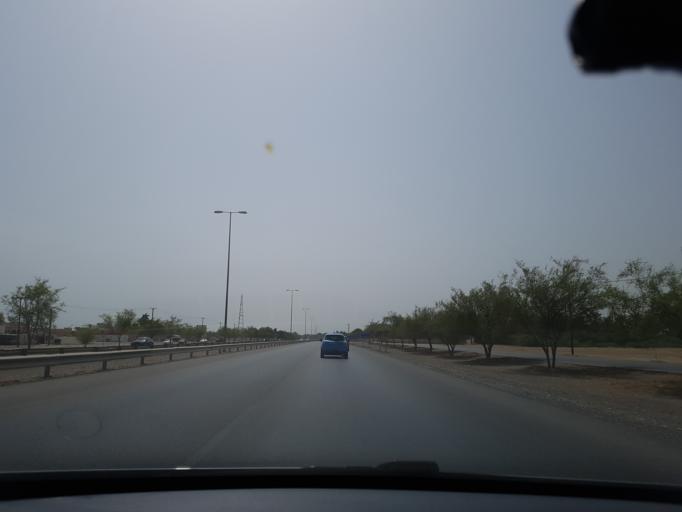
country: OM
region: Al Batinah
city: As Suwayq
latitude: 23.8459
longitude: 57.3612
